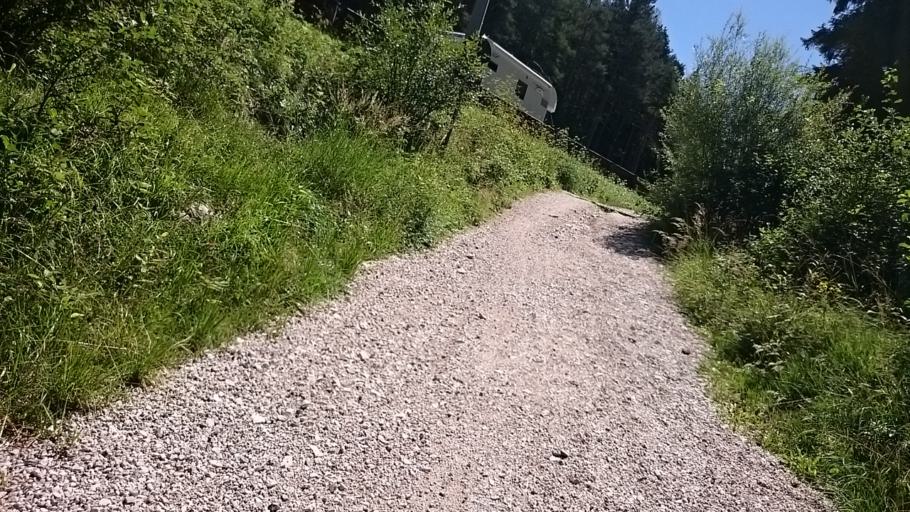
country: IT
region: Veneto
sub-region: Provincia di Belluno
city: San Vito
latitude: 46.4941
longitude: 12.1794
